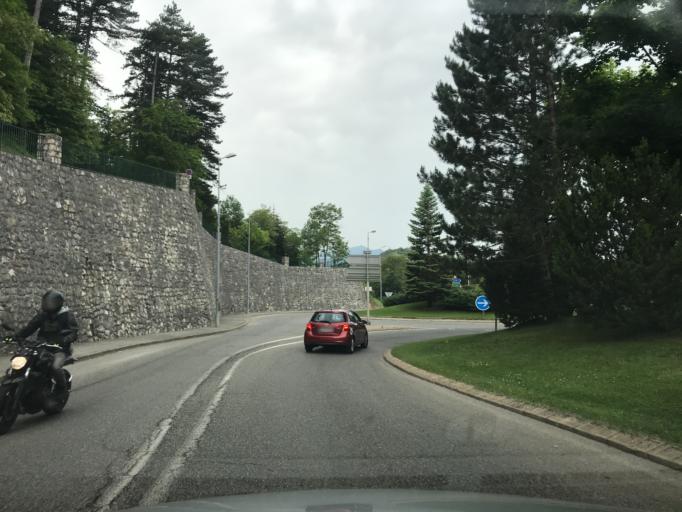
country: FR
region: Provence-Alpes-Cote d'Azur
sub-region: Departement des Alpes-de-Haute-Provence
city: Sisteron
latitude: 44.2005
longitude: 5.9432
